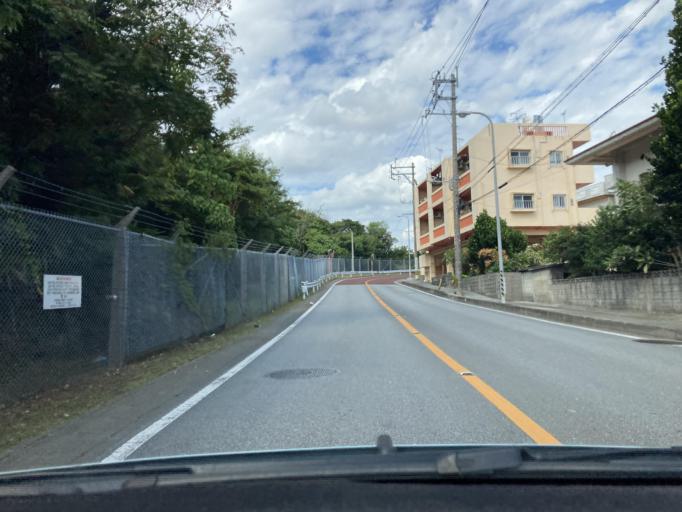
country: JP
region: Okinawa
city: Chatan
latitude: 26.3143
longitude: 127.7672
